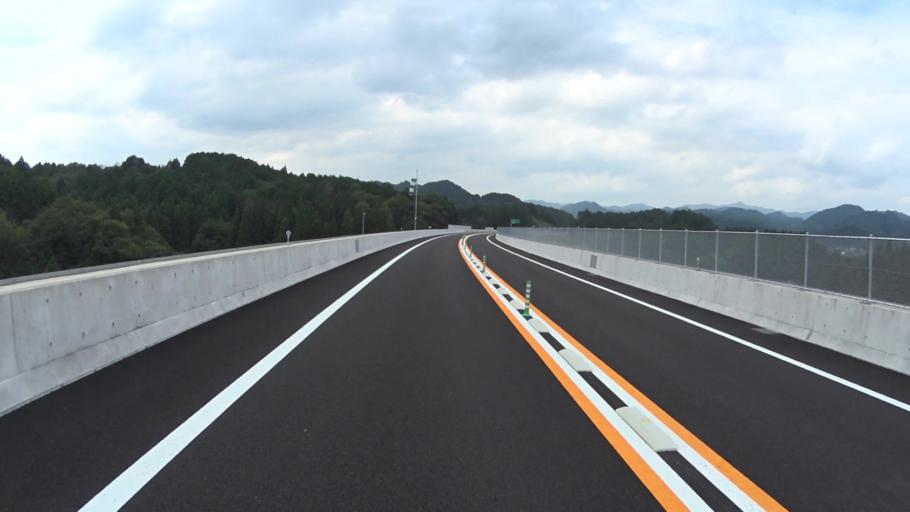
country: JP
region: Kyoto
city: Ayabe
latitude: 35.1713
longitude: 135.3700
